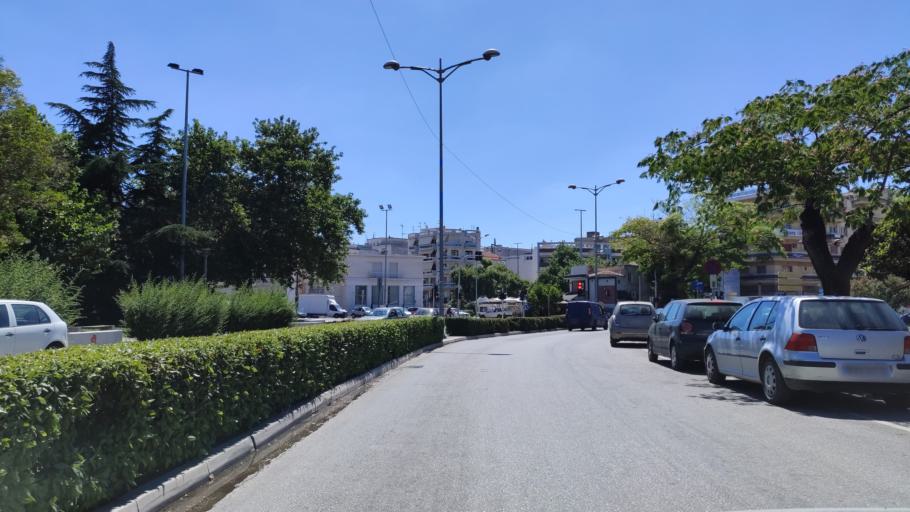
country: GR
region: East Macedonia and Thrace
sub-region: Nomos Rodopis
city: Komotini
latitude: 41.1177
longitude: 25.4067
